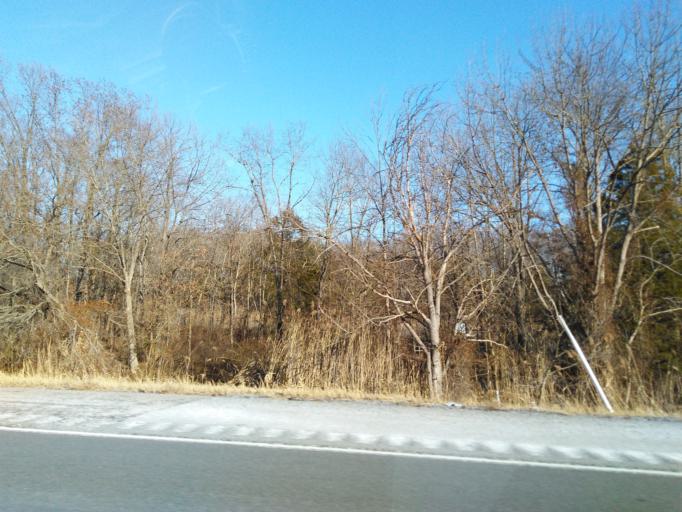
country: US
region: Illinois
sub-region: Franklin County
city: Benton
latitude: 37.9672
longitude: -88.9354
